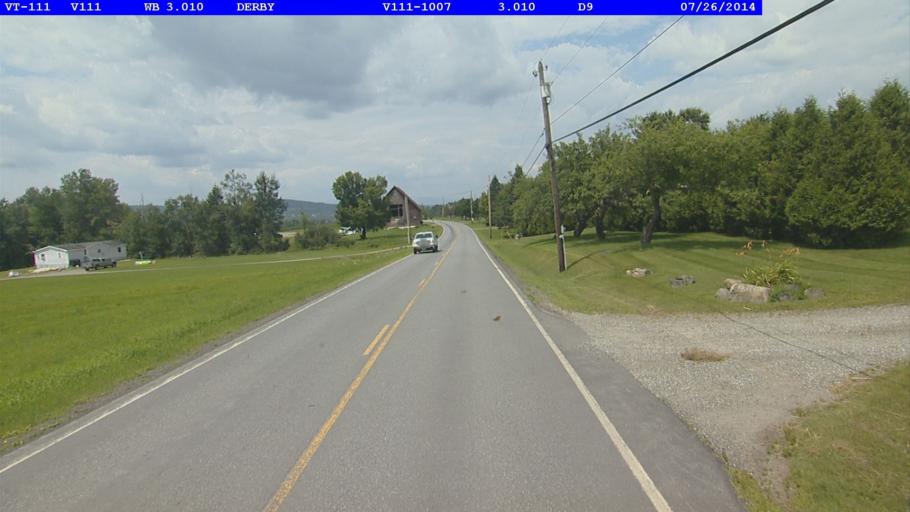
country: US
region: Vermont
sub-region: Orleans County
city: Newport
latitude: 44.9362
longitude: -72.0798
